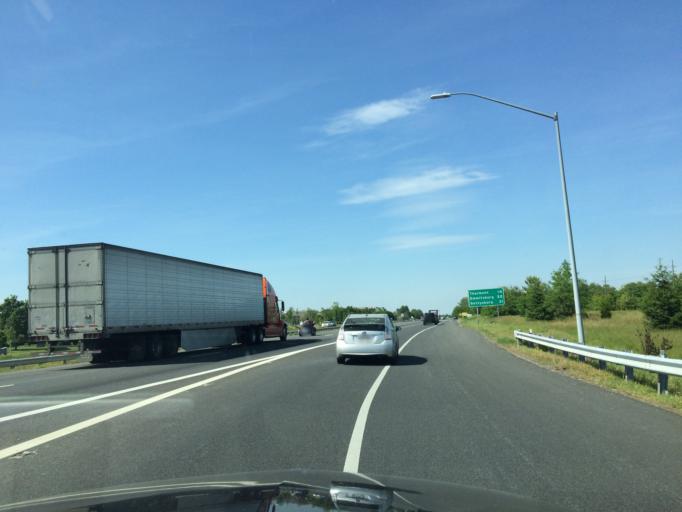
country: US
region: Maryland
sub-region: Frederick County
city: Clover Hill
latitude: 39.4454
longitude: -77.4024
